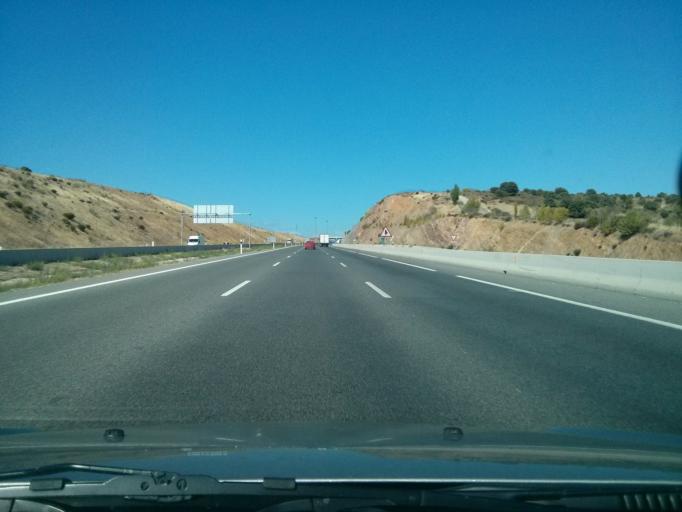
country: ES
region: Madrid
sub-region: Provincia de Madrid
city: El Vellon
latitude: 40.7500
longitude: -3.5850
